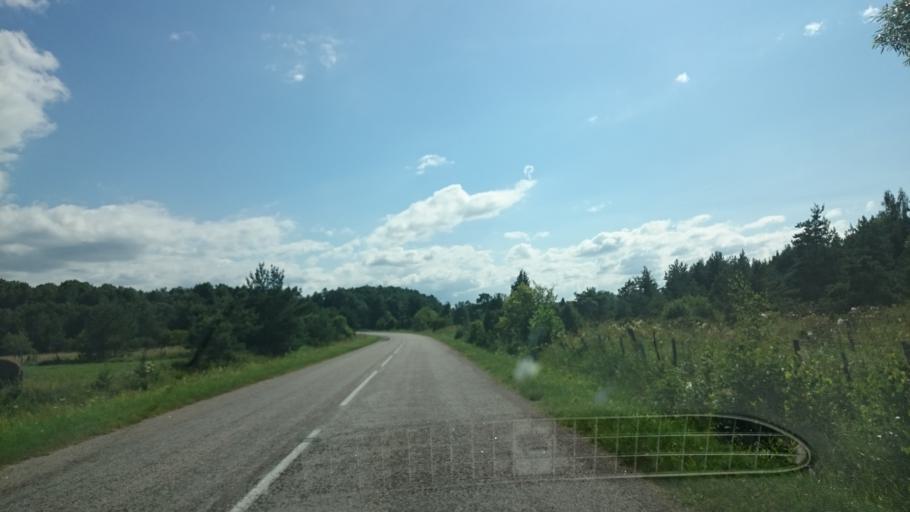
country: EE
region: Saare
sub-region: Orissaare vald
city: Orissaare
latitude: 58.5735
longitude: 22.7617
